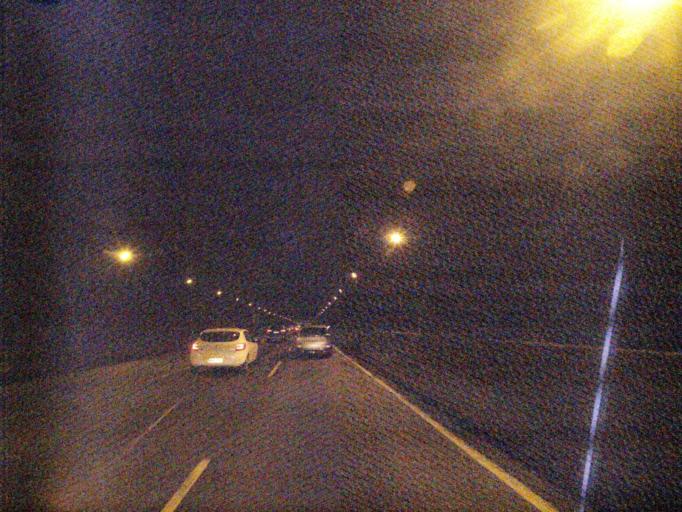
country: BR
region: Rio de Janeiro
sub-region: Rio De Janeiro
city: Rio de Janeiro
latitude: -22.9551
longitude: -43.2053
